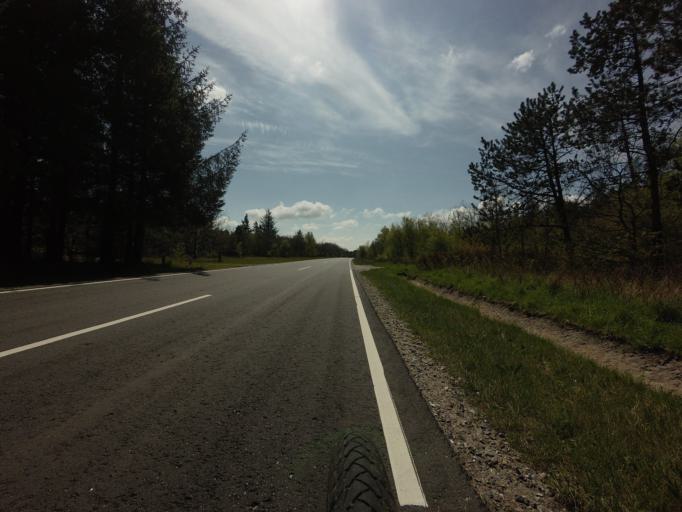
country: DK
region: North Denmark
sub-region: Jammerbugt Kommune
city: Brovst
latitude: 57.1673
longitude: 9.5758
